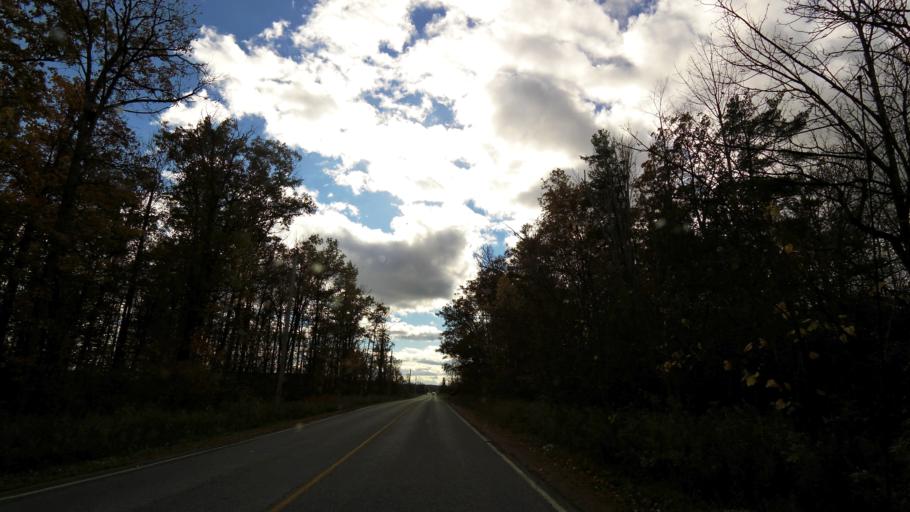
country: CA
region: Ontario
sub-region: Halton
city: Milton
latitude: 43.4611
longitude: -79.8626
